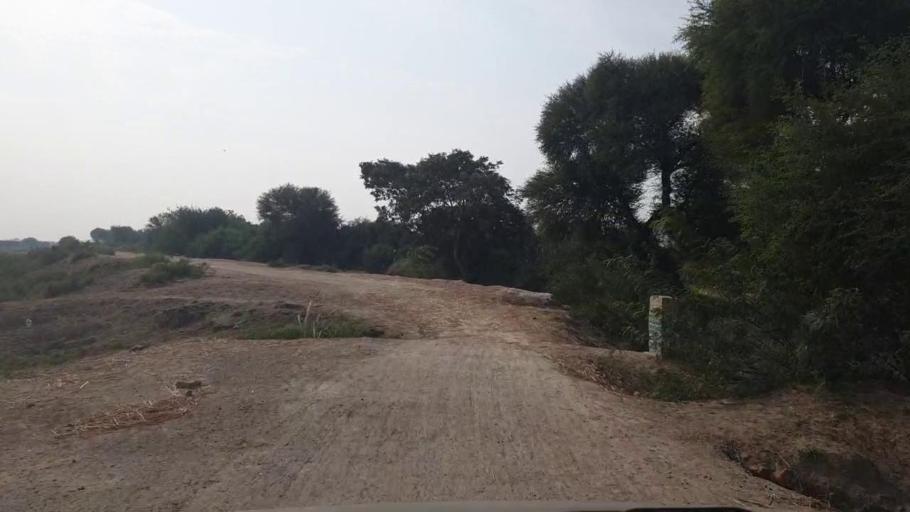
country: PK
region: Sindh
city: Tando Muhammad Khan
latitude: 25.1283
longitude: 68.4908
